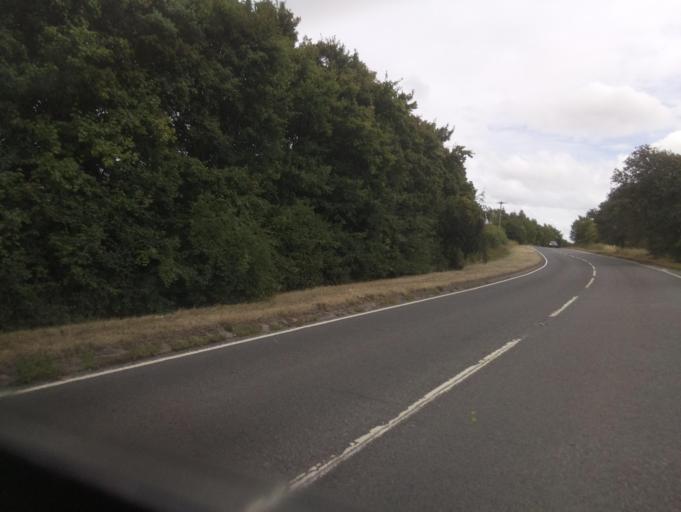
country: GB
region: England
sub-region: Leicestershire
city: Castle Donington
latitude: 52.8027
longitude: -1.3742
